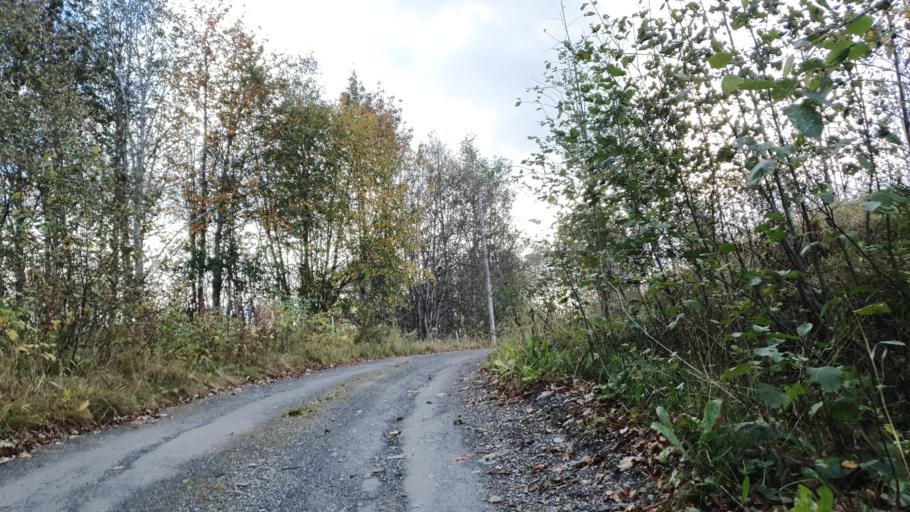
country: NO
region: Sor-Trondelag
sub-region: Klaebu
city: Klaebu
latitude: 63.2886
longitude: 10.4622
